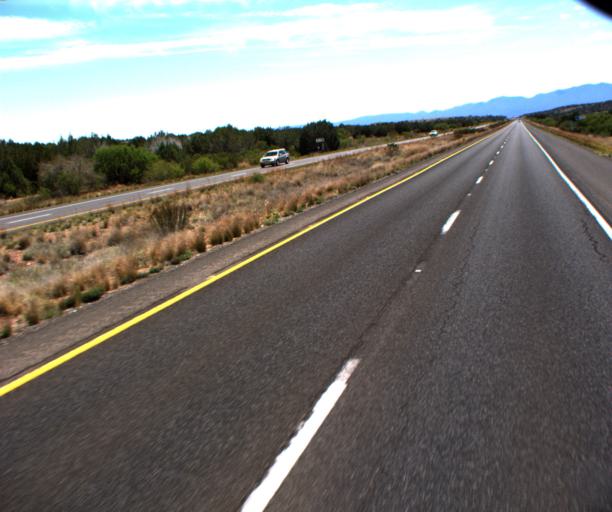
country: US
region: Arizona
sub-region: Yavapai County
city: West Sedona
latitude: 34.8253
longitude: -111.8971
